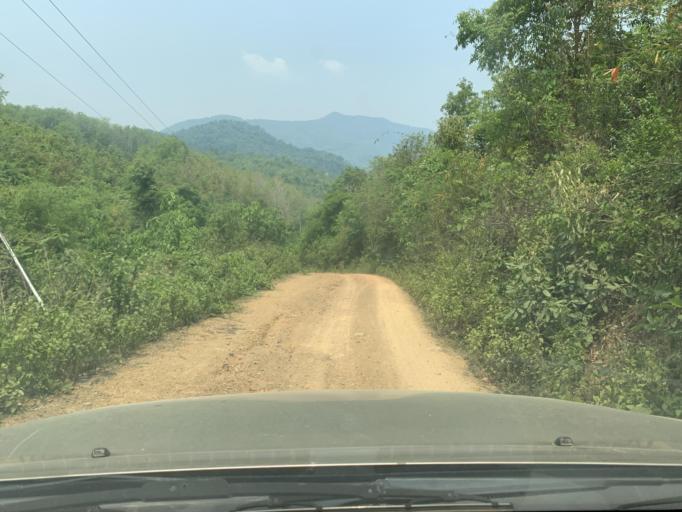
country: LA
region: Louangphabang
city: Louangphabang
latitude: 19.9603
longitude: 102.1283
